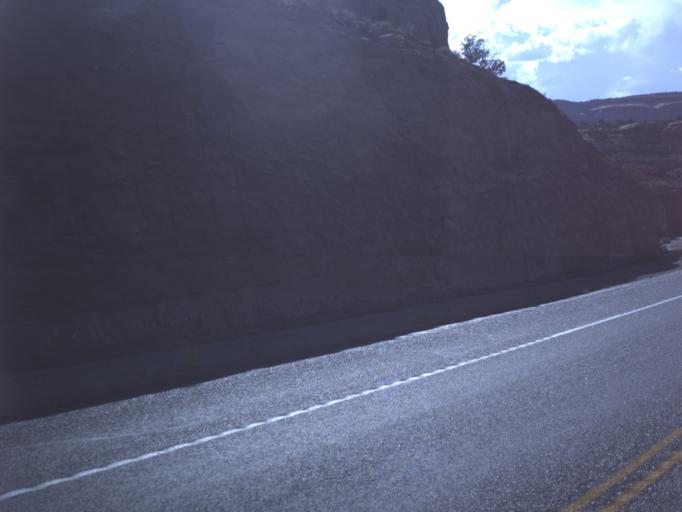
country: US
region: Utah
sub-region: Grand County
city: Moab
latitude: 38.6473
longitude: -109.7348
